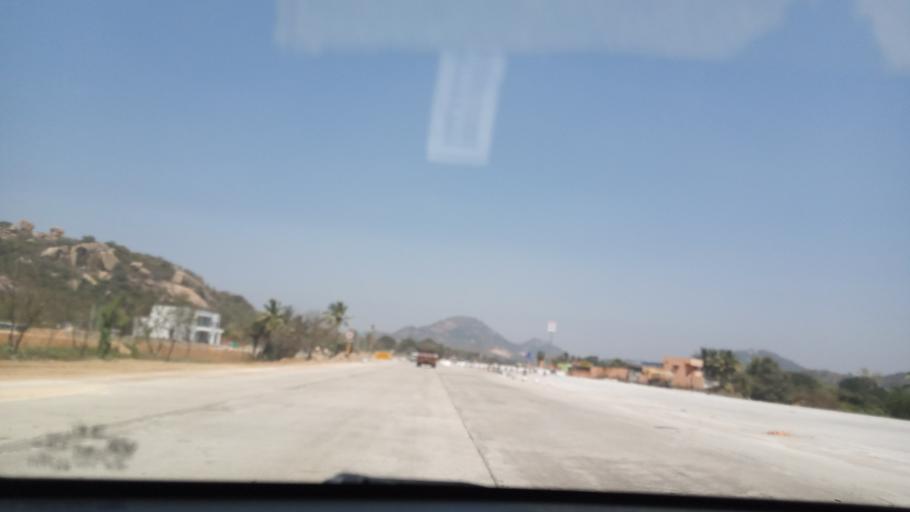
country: IN
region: Andhra Pradesh
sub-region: Chittoor
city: Pakala
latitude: 13.4770
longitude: 79.1864
